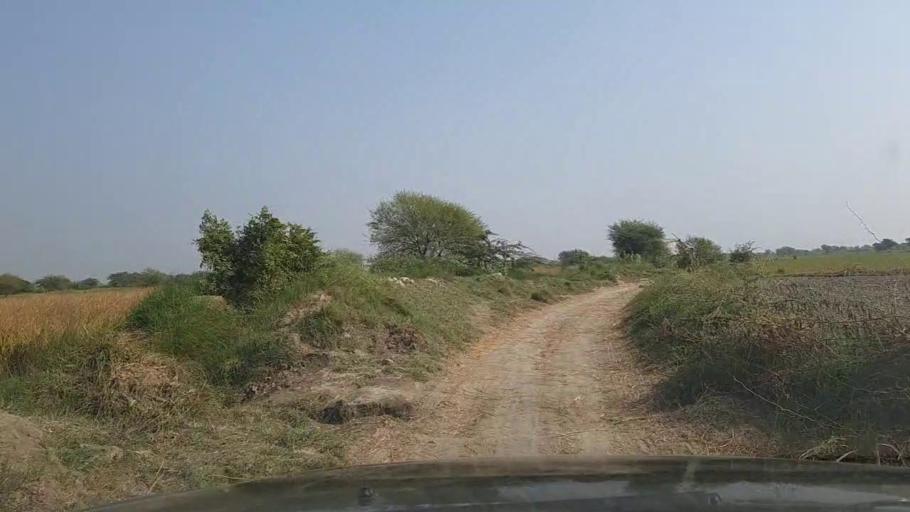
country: PK
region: Sindh
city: Mirpur Batoro
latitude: 24.6803
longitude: 68.2382
